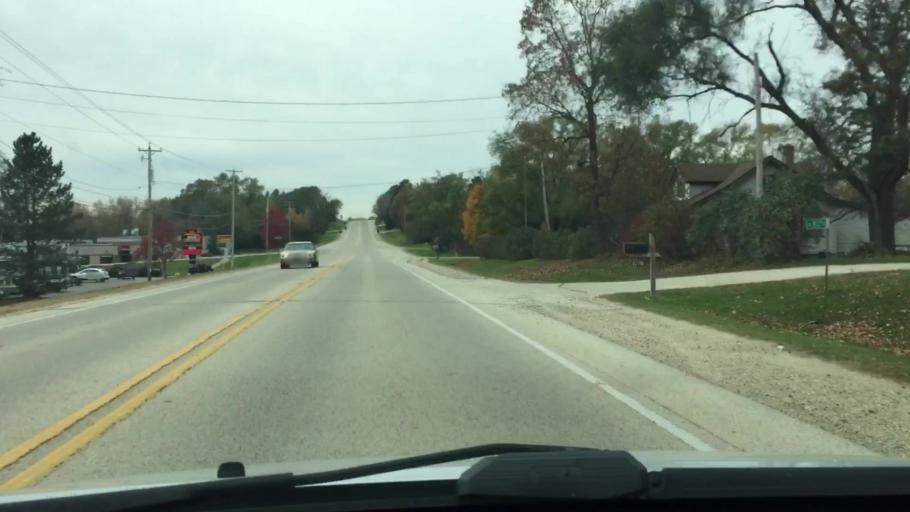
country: US
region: Wisconsin
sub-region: Waukesha County
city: Big Bend
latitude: 42.9203
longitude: -88.2042
